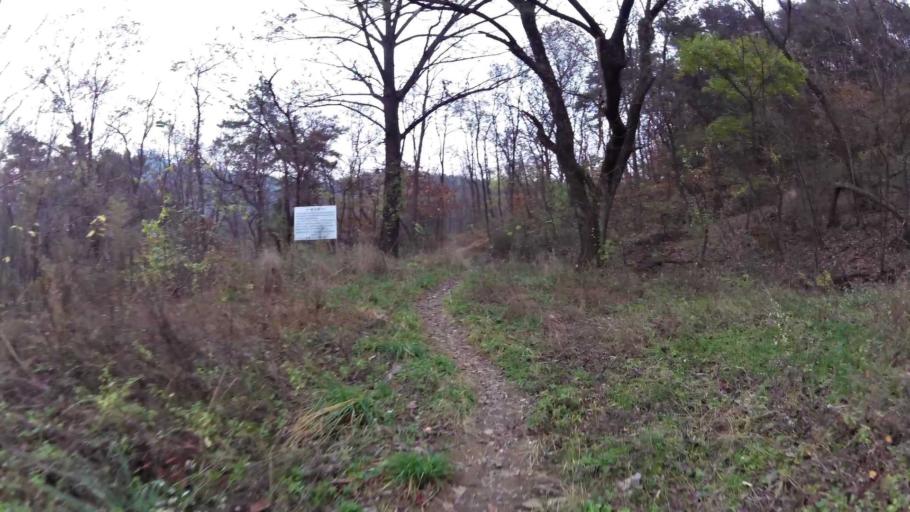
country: KR
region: Daegu
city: Daegu
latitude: 35.8573
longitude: 128.6537
